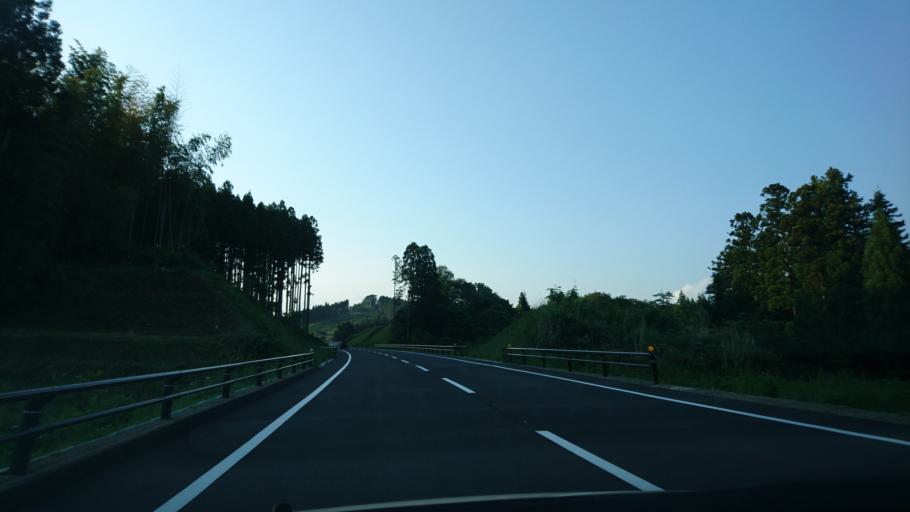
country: JP
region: Iwate
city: Ofunato
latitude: 38.9228
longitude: 141.4560
